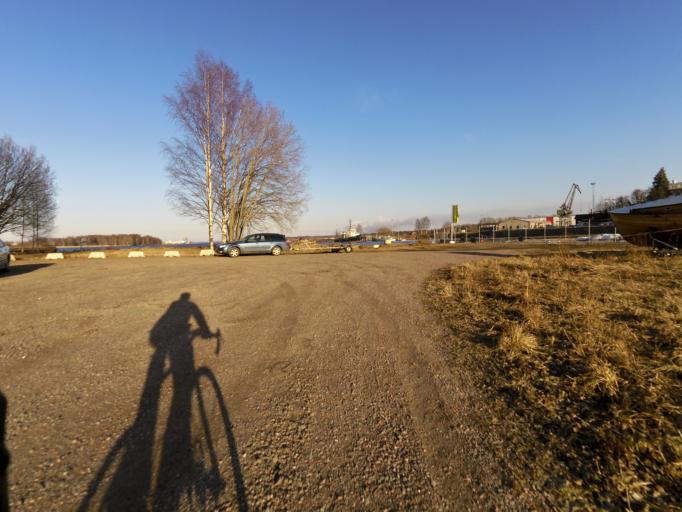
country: SE
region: Gaevleborg
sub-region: Gavle Kommun
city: Gavle
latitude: 60.6800
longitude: 17.1803
